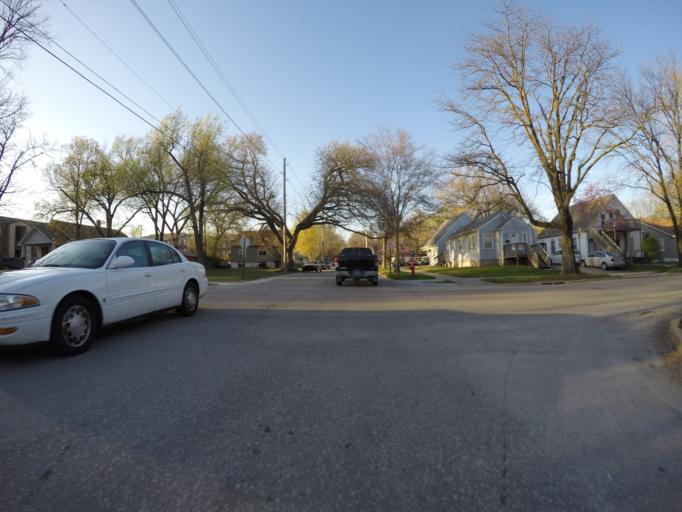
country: US
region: Kansas
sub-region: Riley County
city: Manhattan
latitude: 39.1909
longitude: -96.5731
